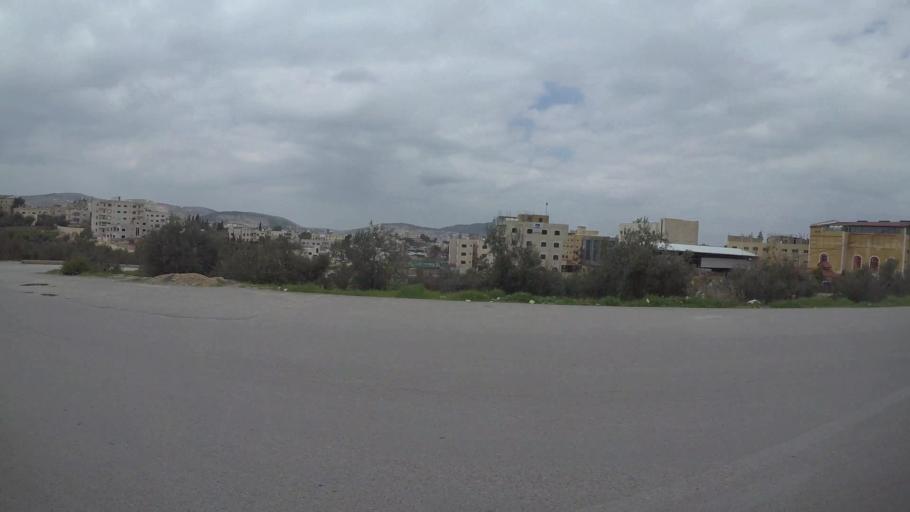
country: JO
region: Amman
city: Al Jubayhah
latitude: 32.0588
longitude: 35.8407
